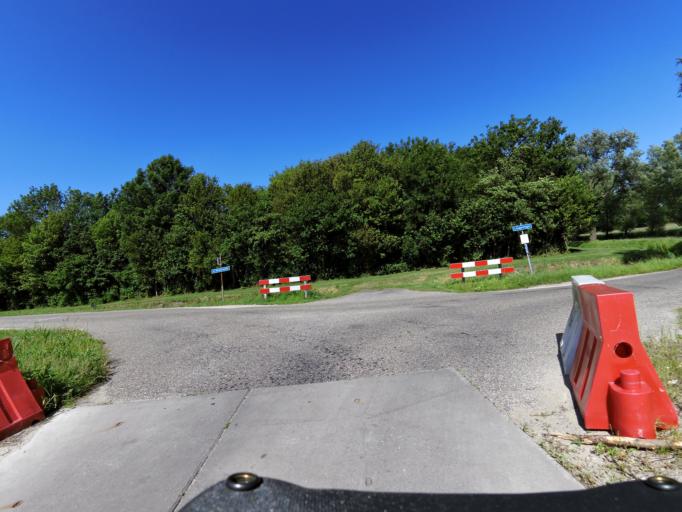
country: NL
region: South Holland
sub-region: Gemeente Brielle
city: Brielle
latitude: 51.9084
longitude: 4.1621
